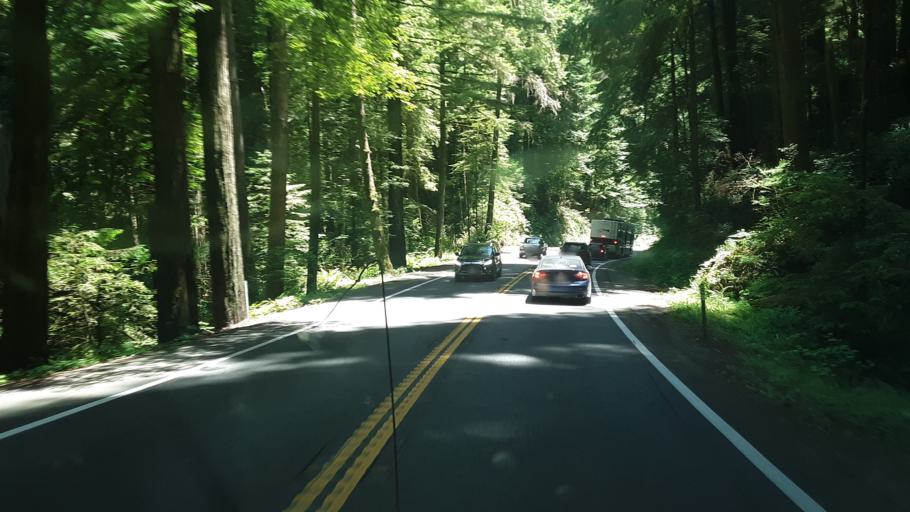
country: US
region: California
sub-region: Del Norte County
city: Bertsch-Oceanview
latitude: 41.8113
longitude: -124.1240
